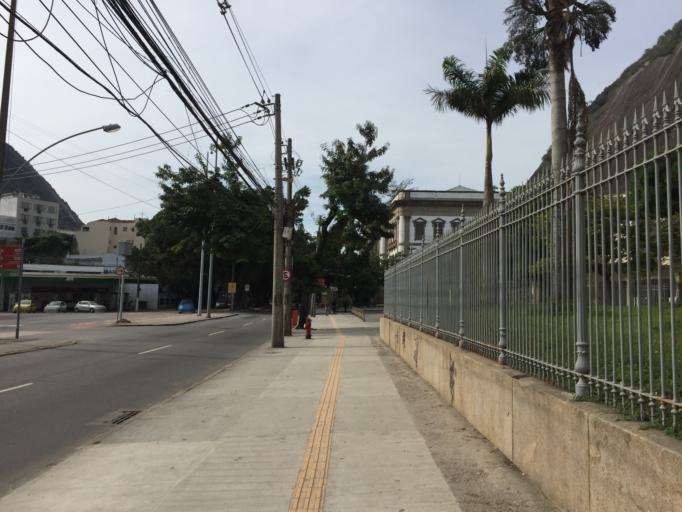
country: BR
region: Rio de Janeiro
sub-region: Rio De Janeiro
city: Rio de Janeiro
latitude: -22.9533
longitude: -43.1717
